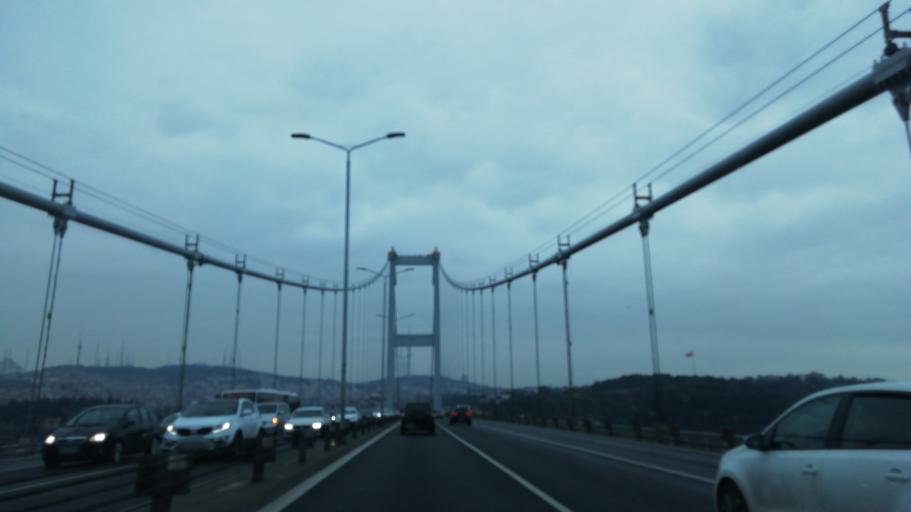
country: TR
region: Istanbul
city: UEskuedar
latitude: 41.0448
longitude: 29.0351
